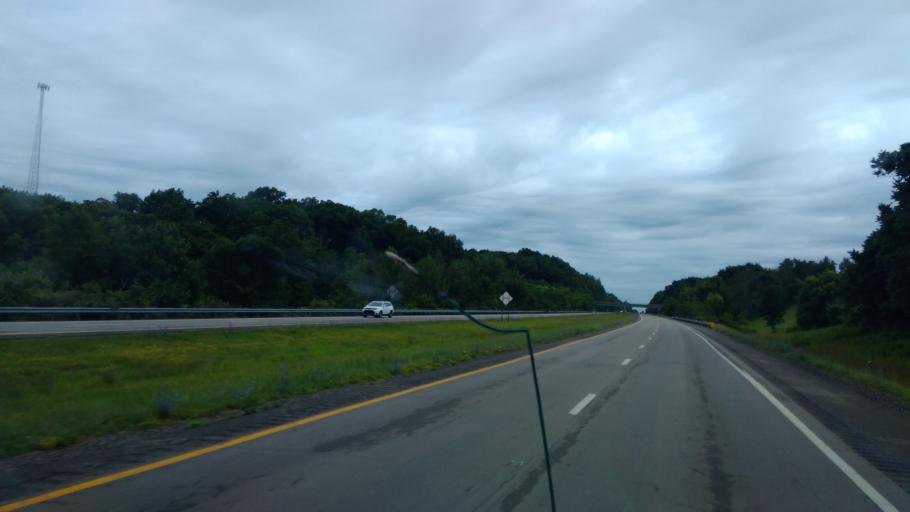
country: US
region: Ohio
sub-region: Columbiana County
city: Lisbon
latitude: 40.7813
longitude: -80.7362
